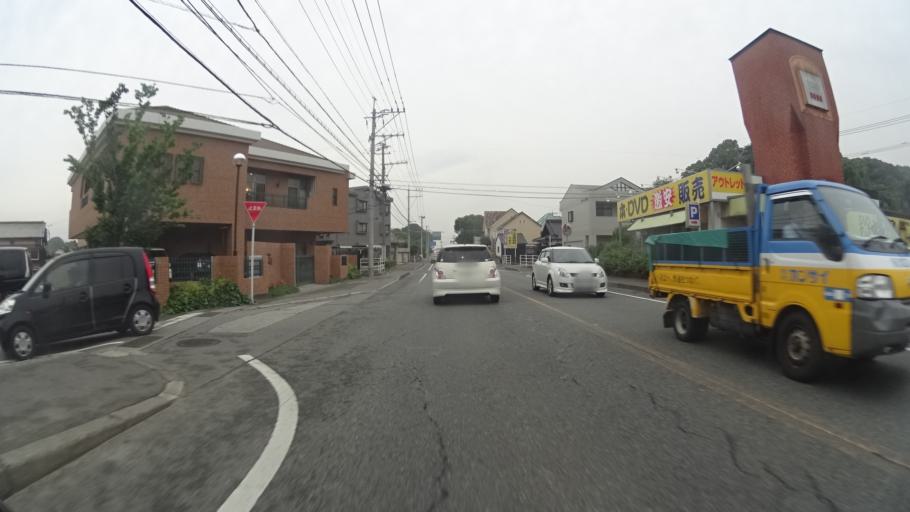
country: JP
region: Fukuoka
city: Dazaifu
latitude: 33.5199
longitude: 130.4999
